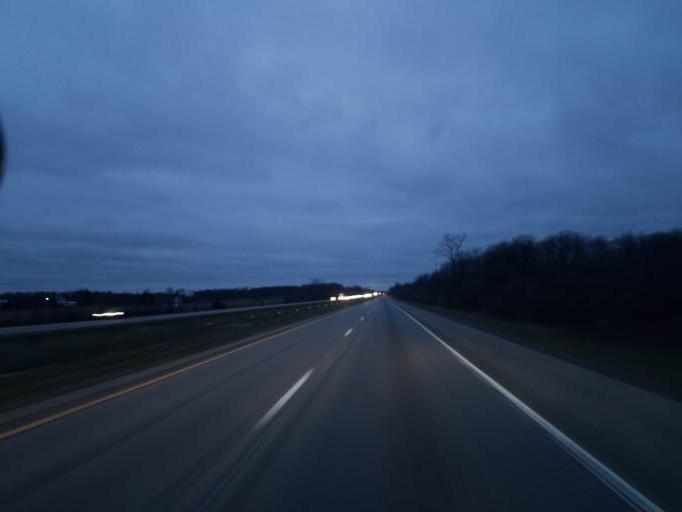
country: US
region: Michigan
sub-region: Washtenaw County
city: Milan
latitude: 42.1244
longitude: -83.6827
